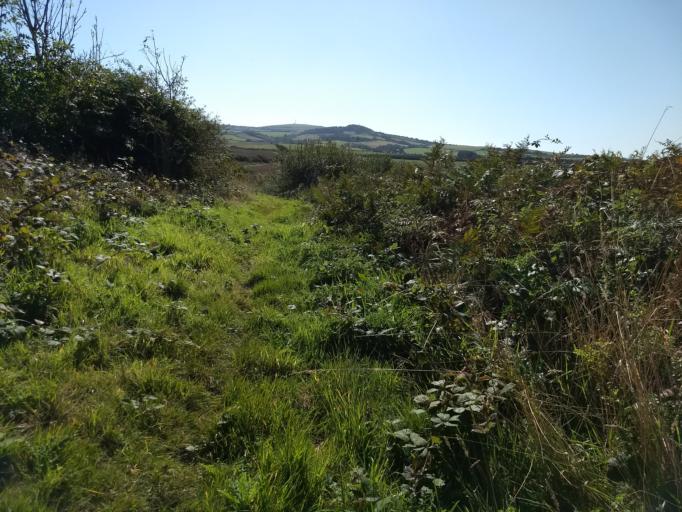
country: GB
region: England
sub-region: Isle of Wight
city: Niton
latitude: 50.6328
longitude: -1.2798
